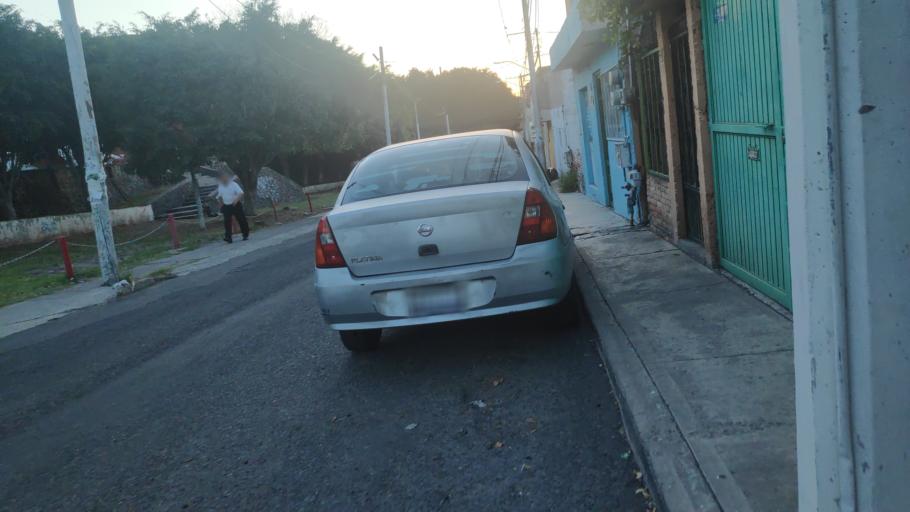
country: MX
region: Queretaro
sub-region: Queretaro
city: Santiago de Queretaro
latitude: 20.5805
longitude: -100.3734
